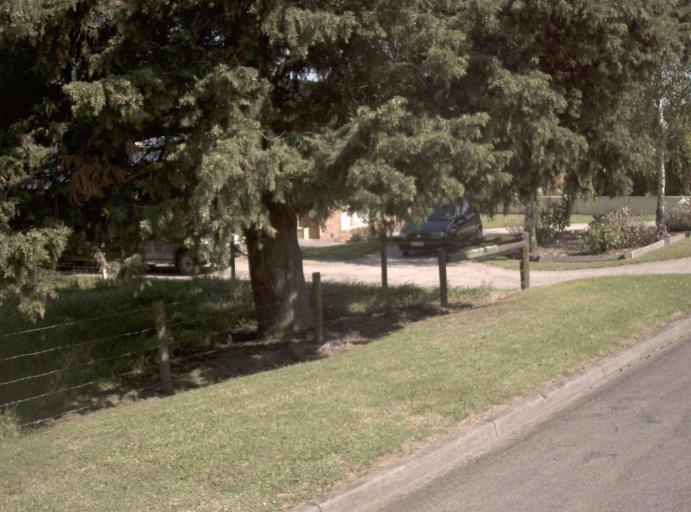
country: AU
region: Victoria
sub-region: Baw Baw
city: Warragul
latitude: -38.3381
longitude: 145.7659
